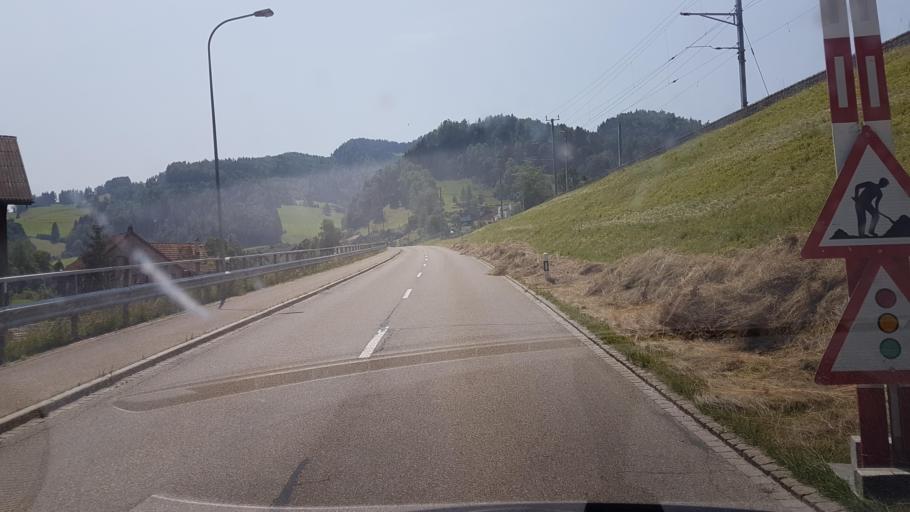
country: CH
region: Saint Gallen
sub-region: Wahlkreis Toggenburg
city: Mogelsberg
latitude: 47.3403
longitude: 9.1315
